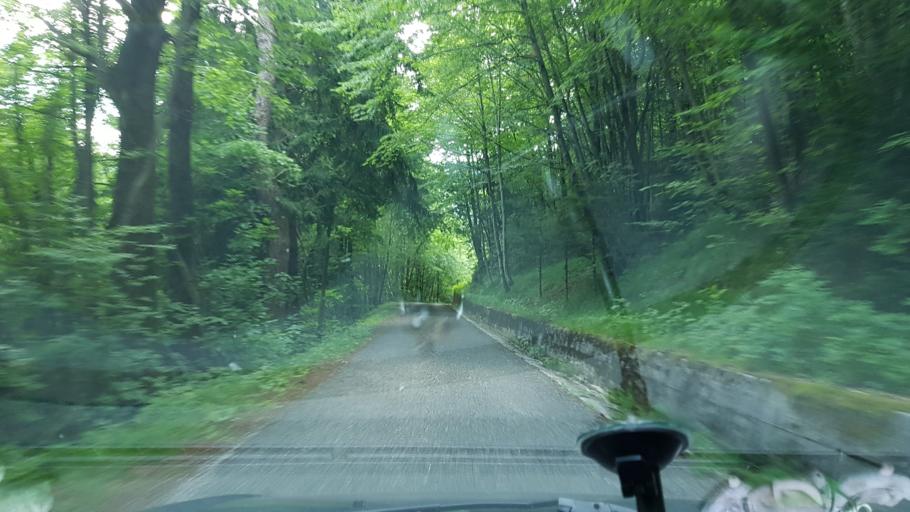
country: IT
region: Friuli Venezia Giulia
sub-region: Provincia di Udine
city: Prato
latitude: 46.3451
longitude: 13.3990
